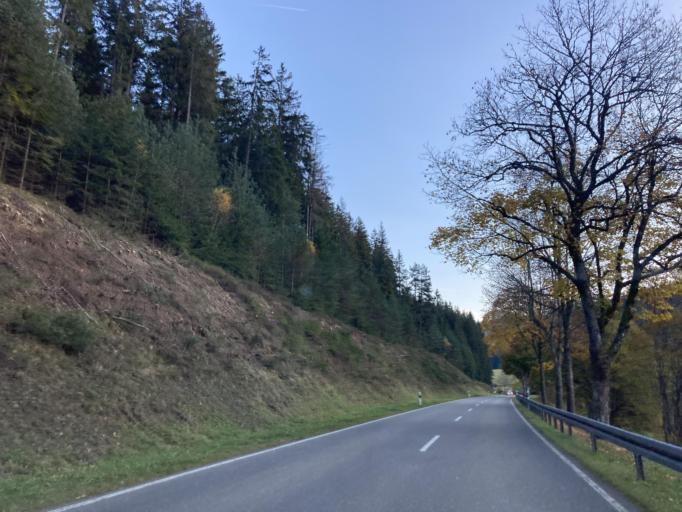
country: DE
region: Baden-Wuerttemberg
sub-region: Freiburg Region
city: Vohrenbach
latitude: 48.0009
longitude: 8.3034
